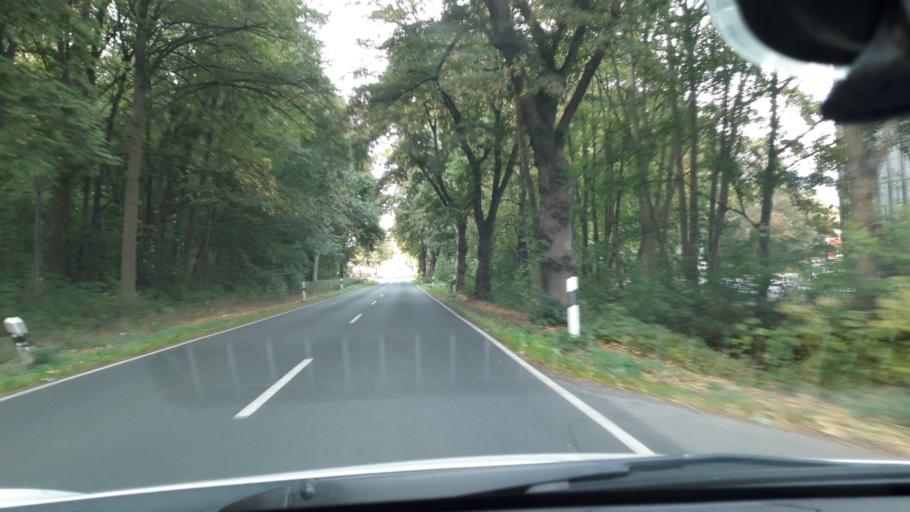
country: DE
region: Lower Saxony
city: Alt Wallmoden
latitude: 52.0350
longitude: 10.3204
